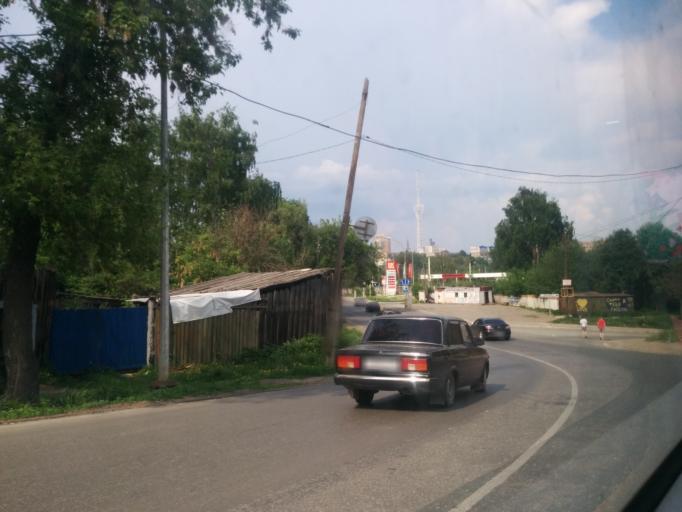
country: RU
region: Perm
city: Perm
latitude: 58.0146
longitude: 56.2633
